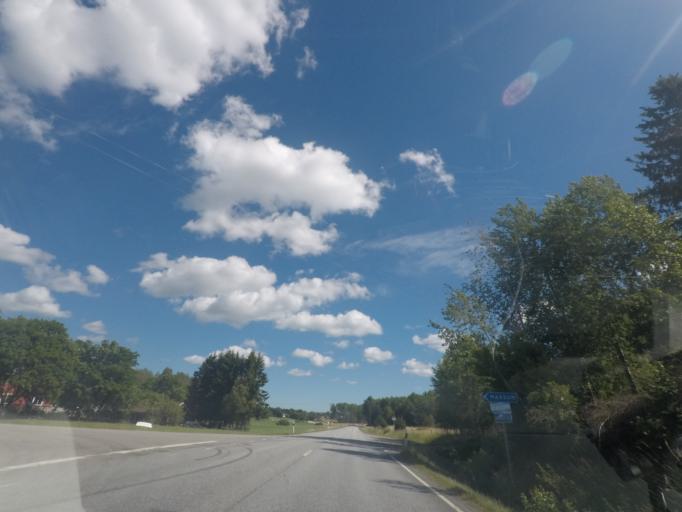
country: SE
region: Stockholm
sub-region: Norrtalje Kommun
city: Hallstavik
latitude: 59.9516
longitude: 18.7641
